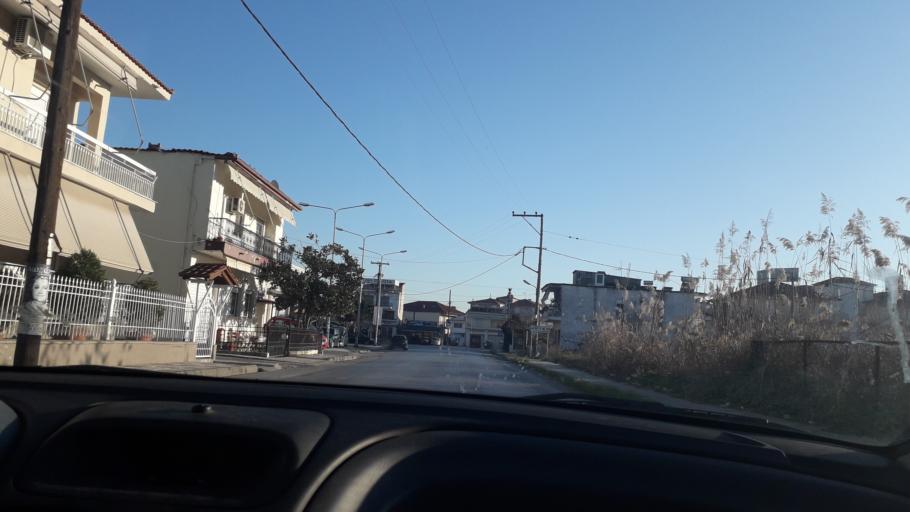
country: GR
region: Central Macedonia
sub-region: Nomos Imathias
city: Alexandreia
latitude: 40.6329
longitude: 22.4420
